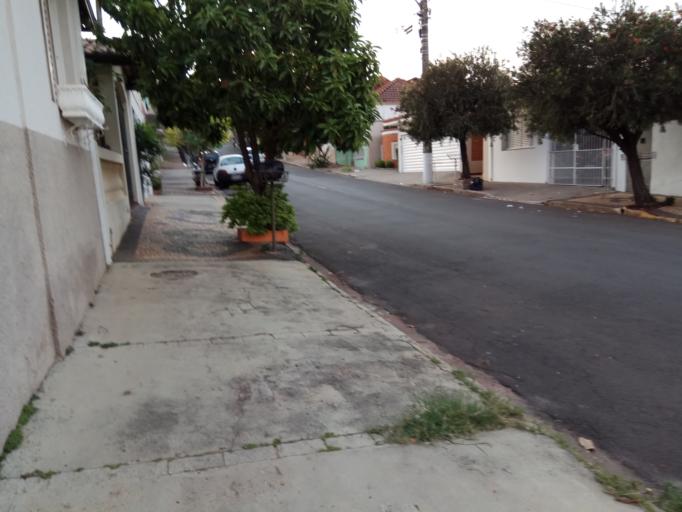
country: BR
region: Sao Paulo
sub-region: Piracicaba
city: Piracicaba
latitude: -22.7095
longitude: -47.6436
